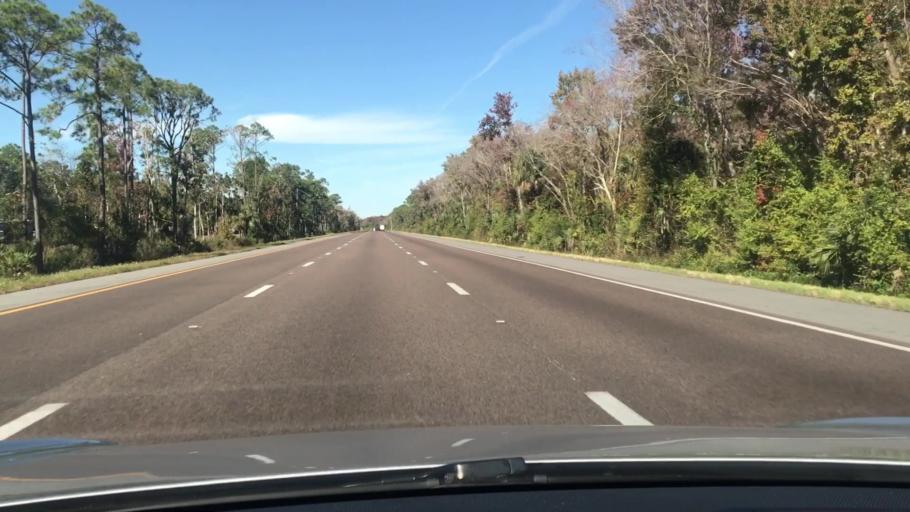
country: US
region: Florida
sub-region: Volusia County
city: Edgewater
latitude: 28.9145
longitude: -80.9353
